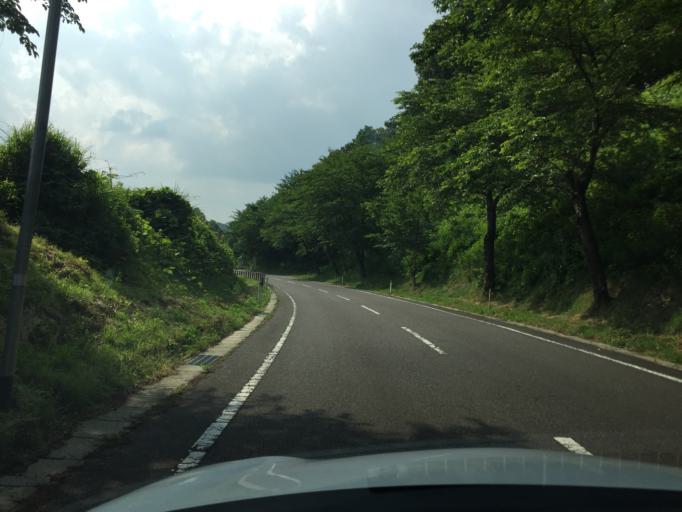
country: JP
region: Fukushima
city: Miharu
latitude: 37.4097
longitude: 140.4943
